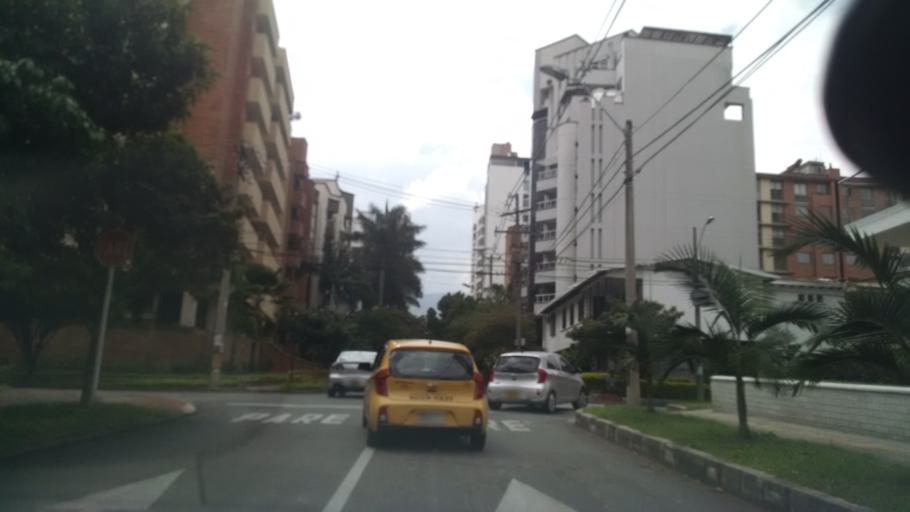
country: CO
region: Antioquia
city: Medellin
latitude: 6.2406
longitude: -75.5975
